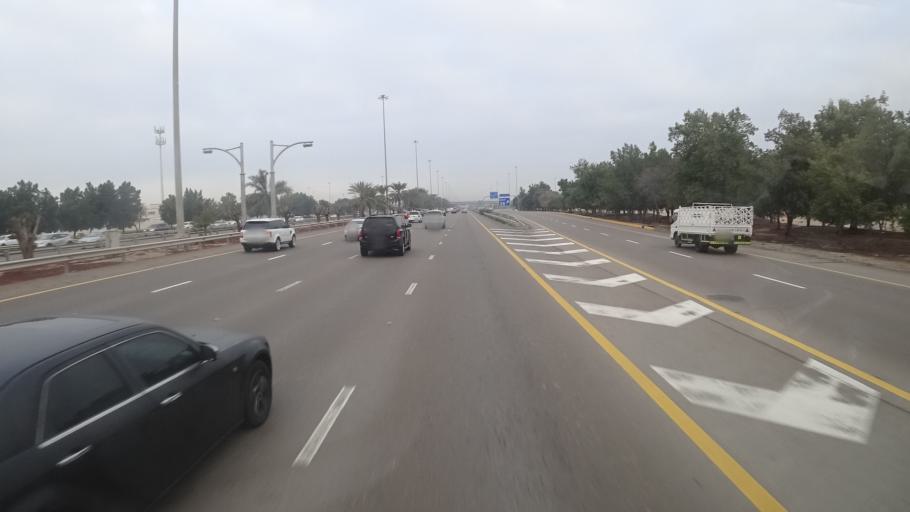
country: AE
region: Abu Dhabi
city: Abu Dhabi
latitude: 24.3703
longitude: 54.5569
